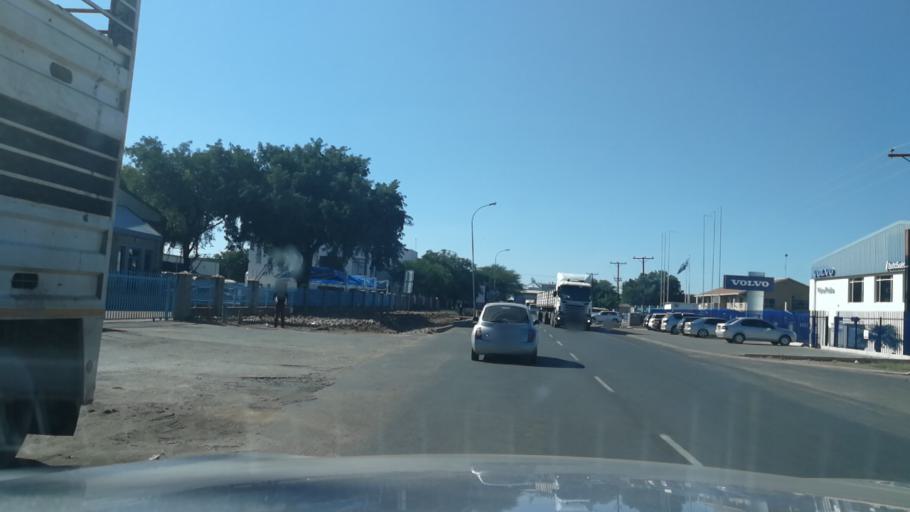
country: BW
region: South East
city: Gaborone
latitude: -24.6926
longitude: 25.8853
